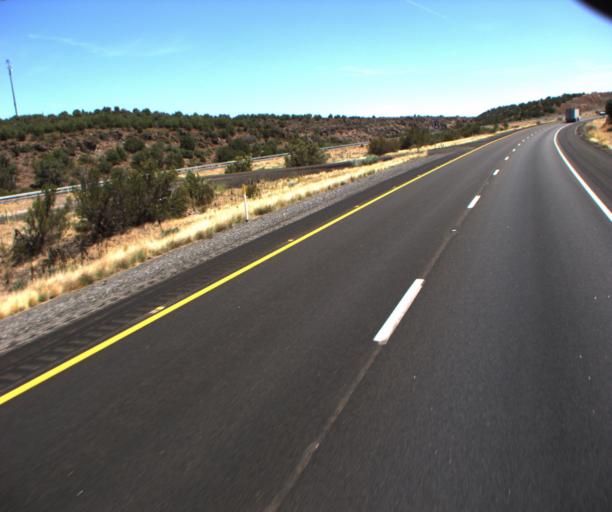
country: US
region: Arizona
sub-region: Mohave County
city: Peach Springs
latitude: 35.1872
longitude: -113.4465
